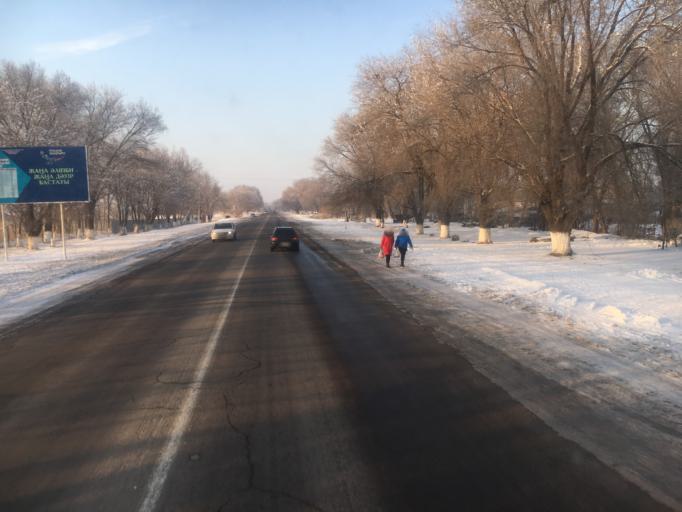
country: KZ
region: Almaty Oblysy
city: Burunday
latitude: 43.3357
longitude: 76.6602
